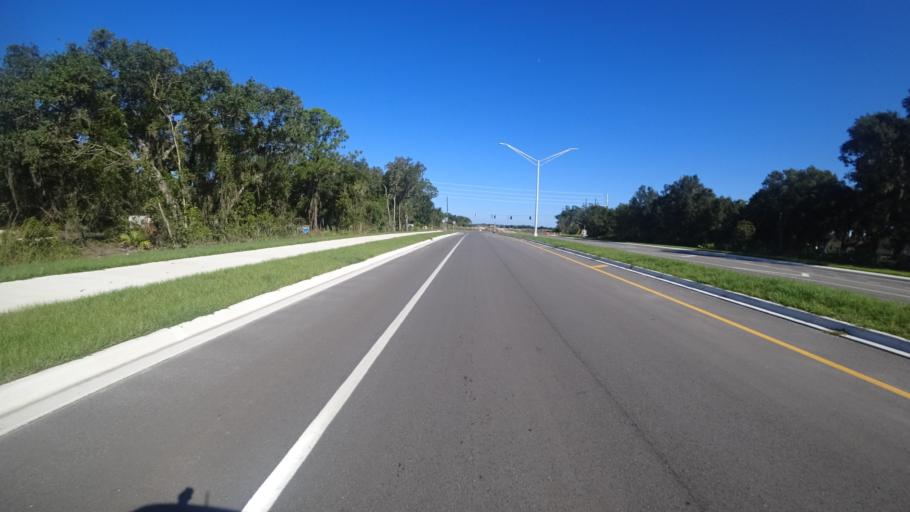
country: US
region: Florida
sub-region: Manatee County
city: Ellenton
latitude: 27.5841
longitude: -82.4357
